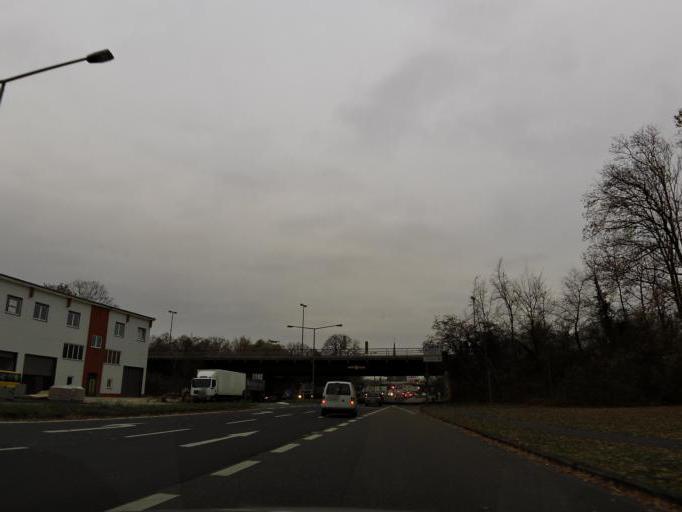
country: DE
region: Hesse
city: Kelsterbach
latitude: 50.0908
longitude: 8.5708
